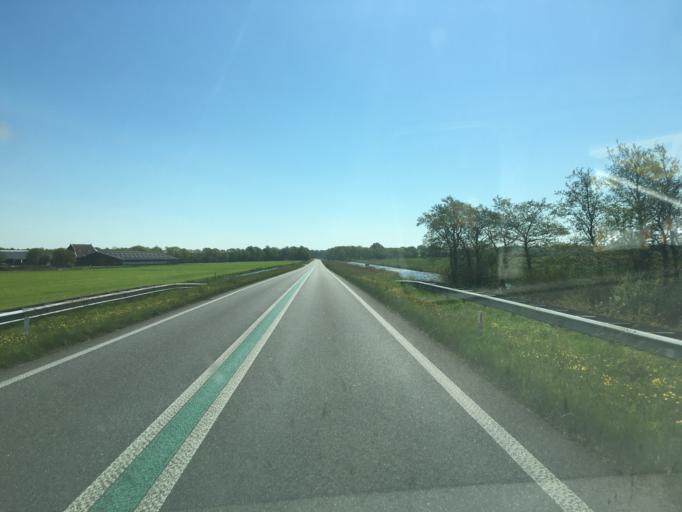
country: NL
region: Friesland
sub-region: Gemeente Gaasterlan-Sleat
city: Oudemirdum
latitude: 52.8798
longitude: 5.5018
